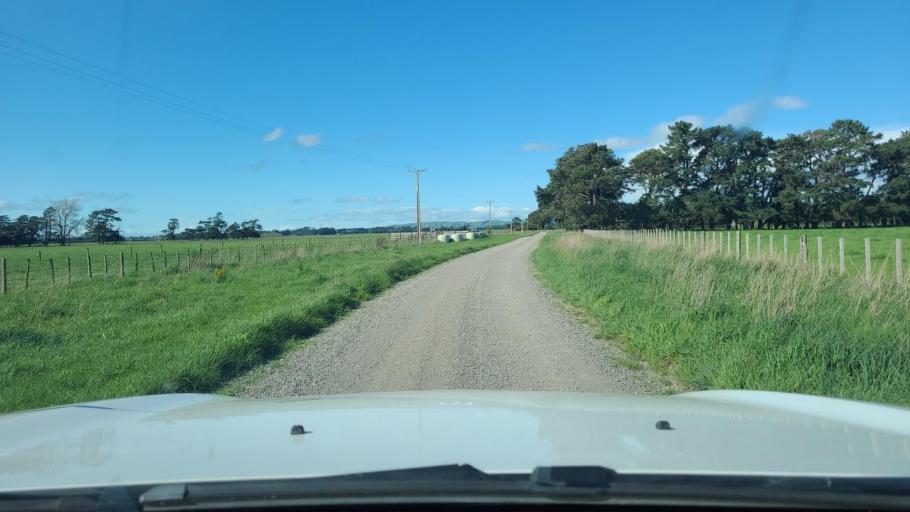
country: NZ
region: Wellington
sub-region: South Wairarapa District
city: Waipawa
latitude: -41.1866
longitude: 175.3632
